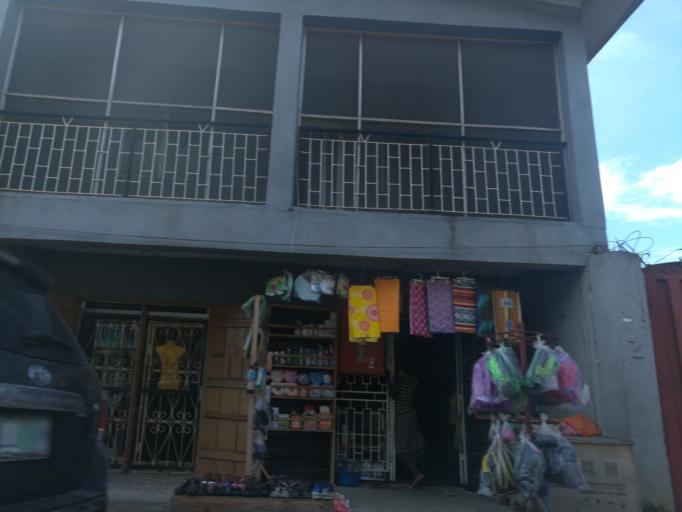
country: NG
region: Lagos
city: Somolu
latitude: 6.5424
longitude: 3.3783
